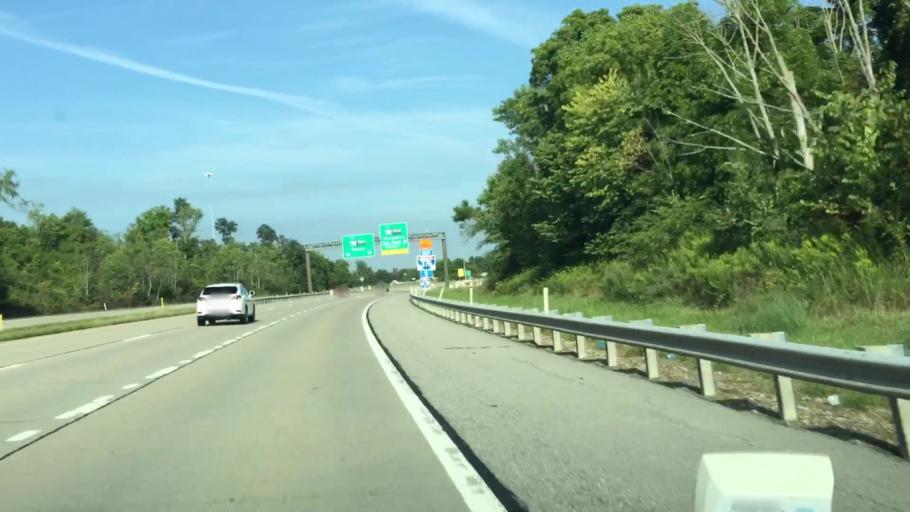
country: US
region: Pennsylvania
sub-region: Allegheny County
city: Carnot-Moon
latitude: 40.5094
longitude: -80.2640
